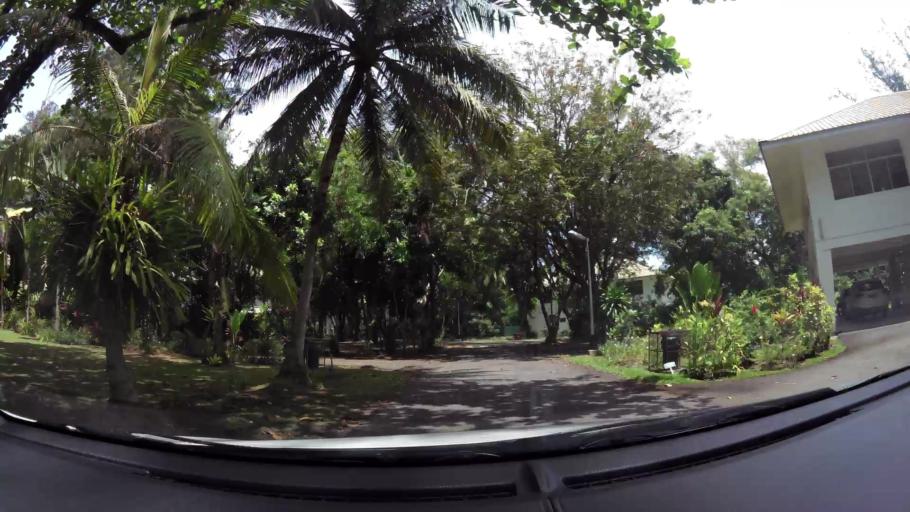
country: BN
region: Belait
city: Kuala Belait
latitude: 4.5978
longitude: 114.2552
